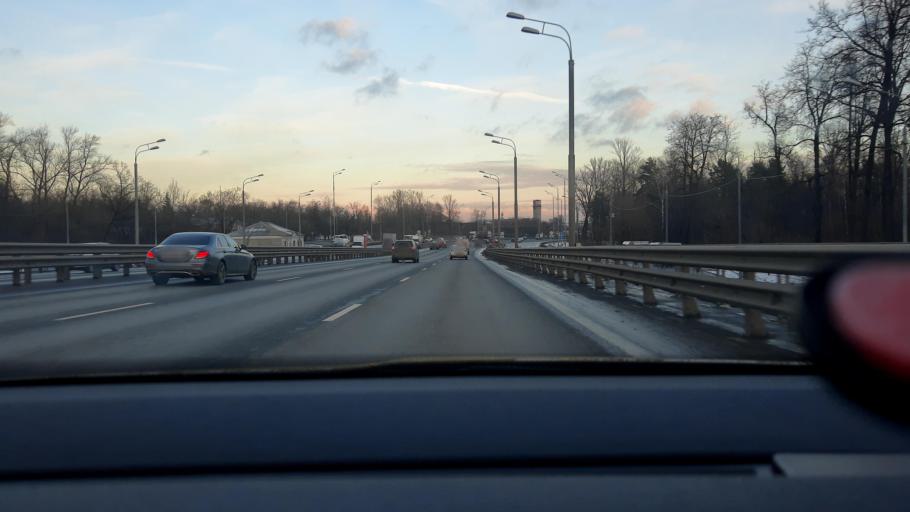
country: RU
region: Moskovskaya
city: Saltykovka
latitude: 55.7920
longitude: 37.9027
